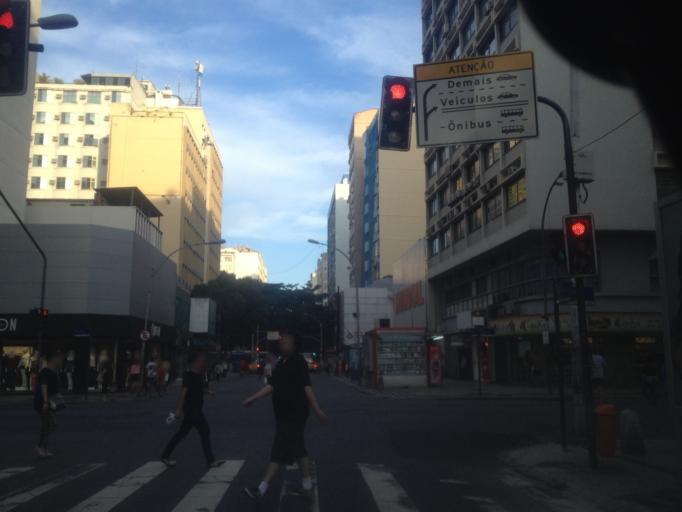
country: BR
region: Rio de Janeiro
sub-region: Rio De Janeiro
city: Rio de Janeiro
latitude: -22.9680
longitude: -43.1855
